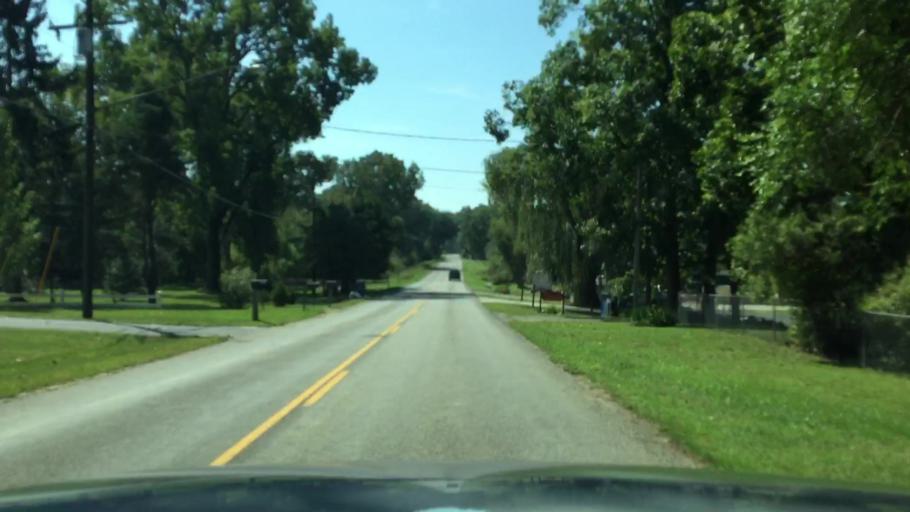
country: US
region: Michigan
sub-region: Lenawee County
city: Manitou Beach-Devils Lake
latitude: 41.9949
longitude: -84.2808
